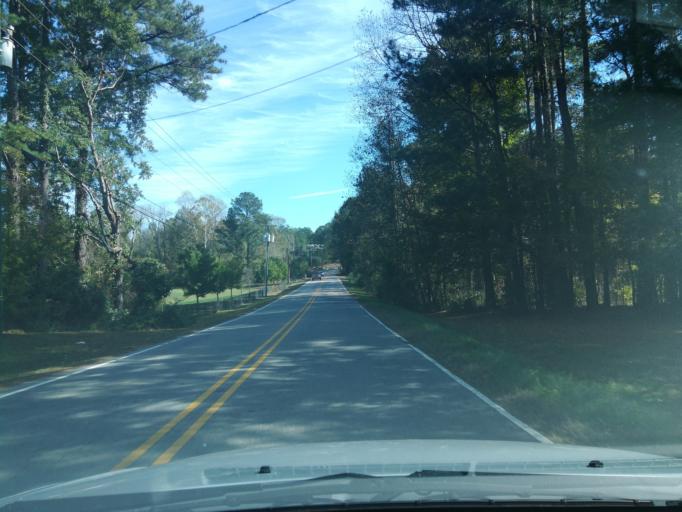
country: US
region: North Carolina
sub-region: Durham County
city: Durham
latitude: 35.9755
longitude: -78.9680
